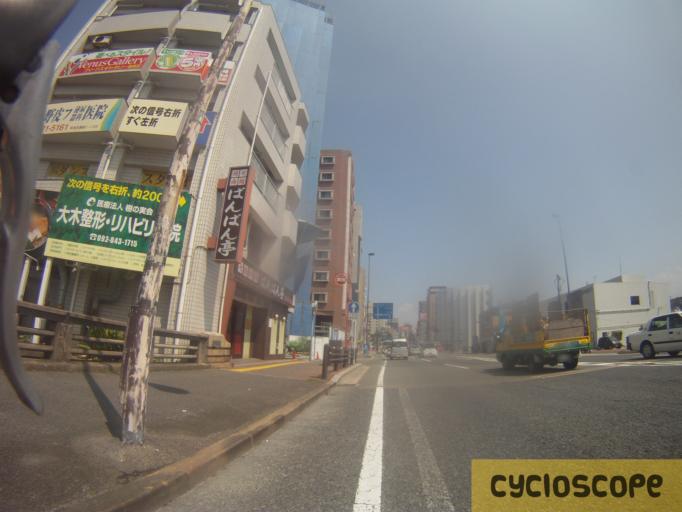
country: JP
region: Fukuoka
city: Fukuoka-shi
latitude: 33.5814
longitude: 130.3489
